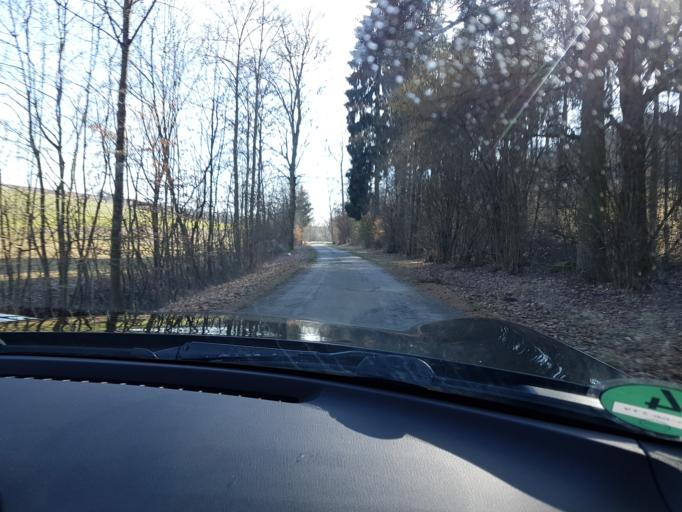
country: DE
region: Baden-Wuerttemberg
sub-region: Karlsruhe Region
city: Rosenberg
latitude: 49.4191
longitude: 9.4978
